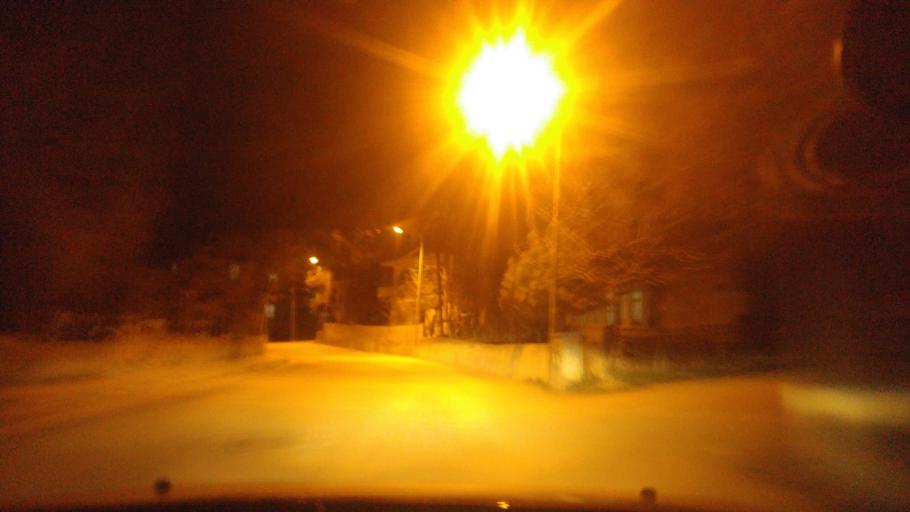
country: TR
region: Karabuk
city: Safranbolu
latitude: 41.2635
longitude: 32.6811
